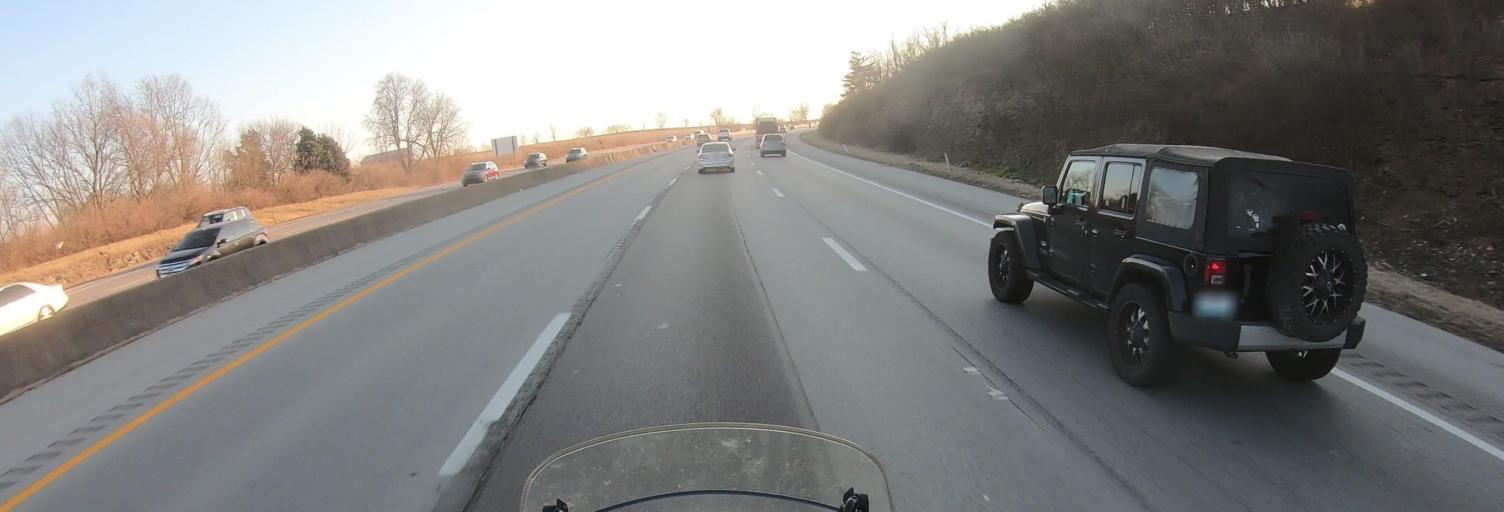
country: US
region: Kentucky
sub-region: Scott County
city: Georgetown
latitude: 38.1924
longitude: -84.5253
